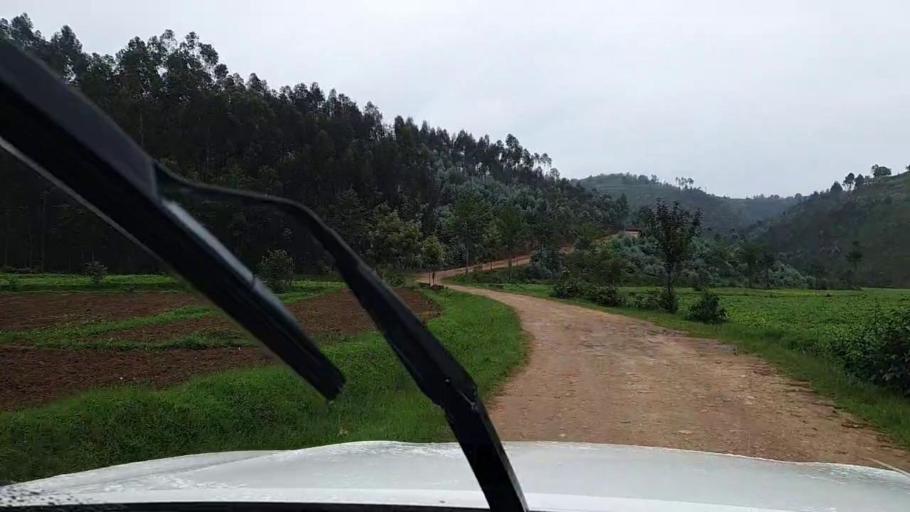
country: RW
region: Southern Province
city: Nzega
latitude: -2.4698
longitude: 29.5027
